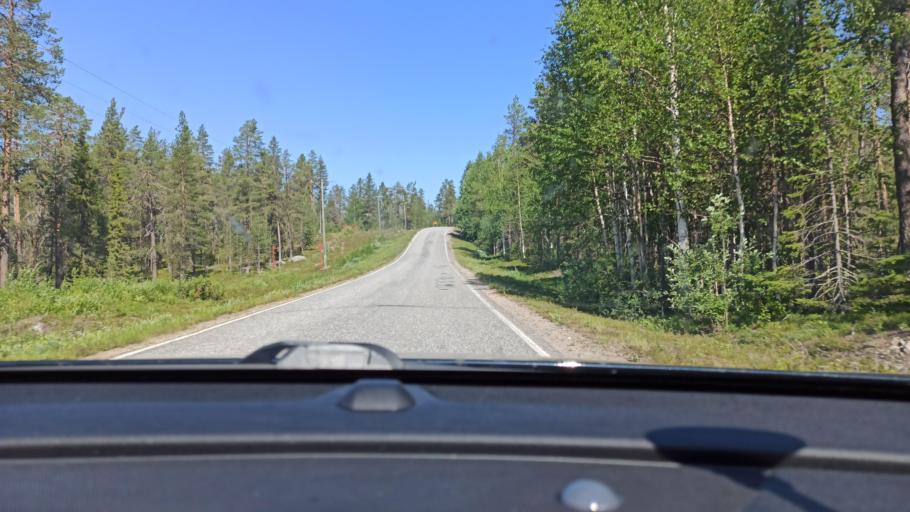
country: FI
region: Lapland
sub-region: Tunturi-Lappi
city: Kolari
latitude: 67.6356
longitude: 24.1582
